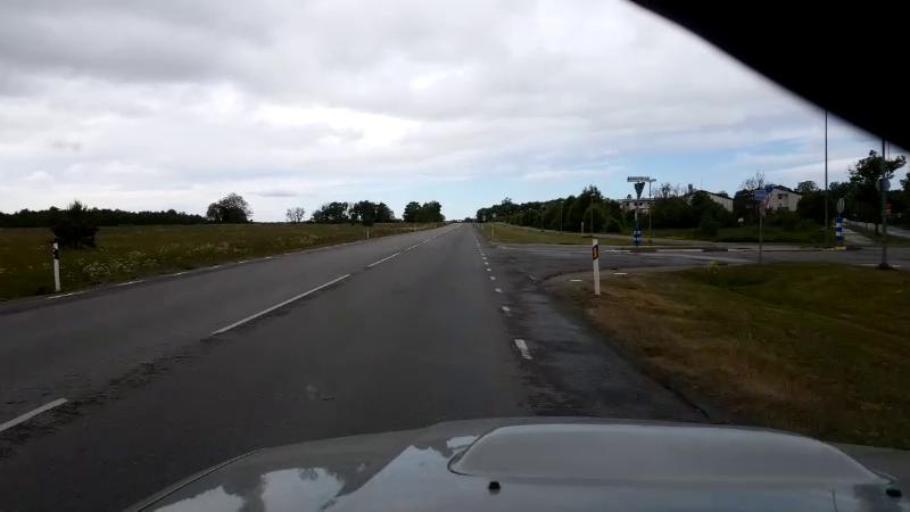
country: EE
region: Harju
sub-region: Harku vald
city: Tabasalu
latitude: 59.4547
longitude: 24.4382
